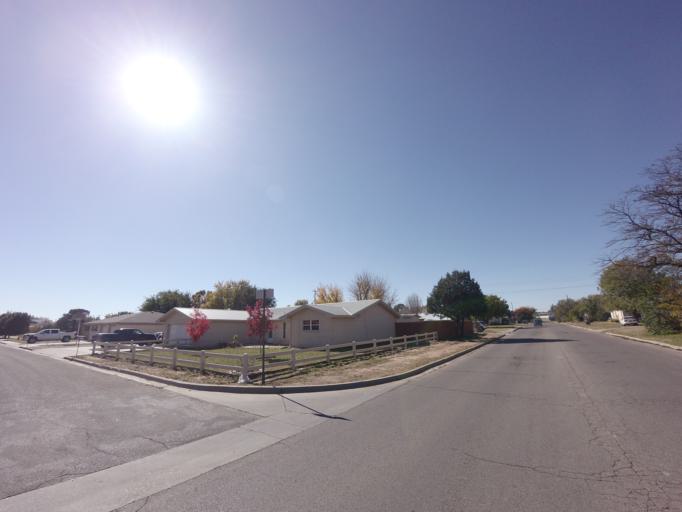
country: US
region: New Mexico
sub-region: Curry County
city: Clovis
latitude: 34.4267
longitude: -103.1980
